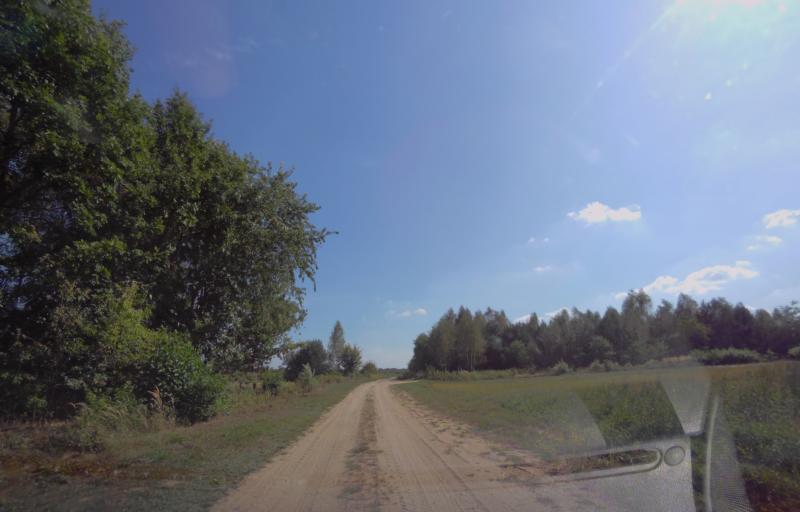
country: PL
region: Subcarpathian Voivodeship
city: Nowa Sarzyna
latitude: 50.2982
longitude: 22.3179
